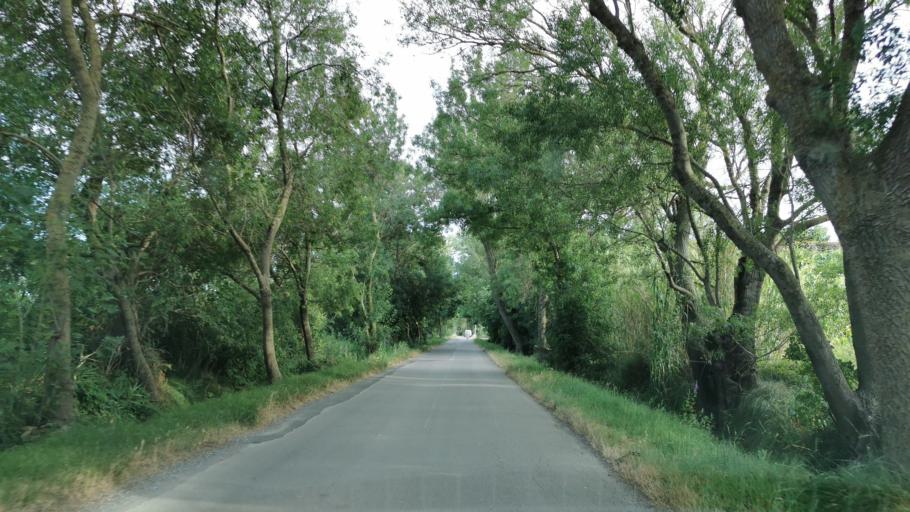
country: FR
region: Languedoc-Roussillon
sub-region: Departement de l'Aude
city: Narbonne
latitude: 43.2067
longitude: 2.9986
